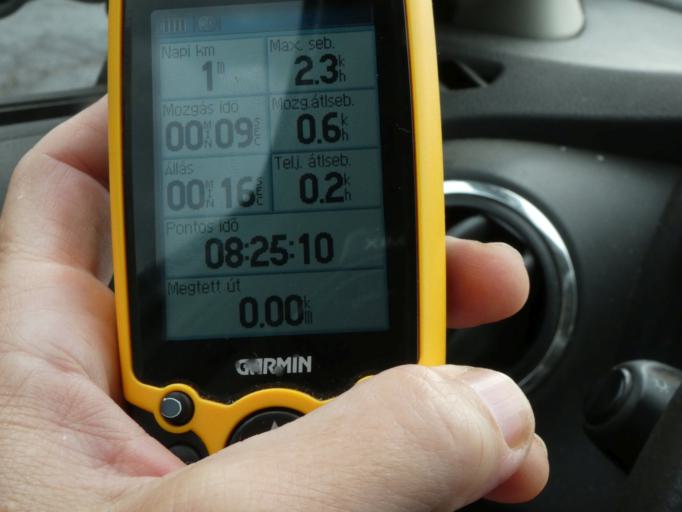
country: HU
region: Pest
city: Csemo
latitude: 47.1253
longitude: 19.6804
